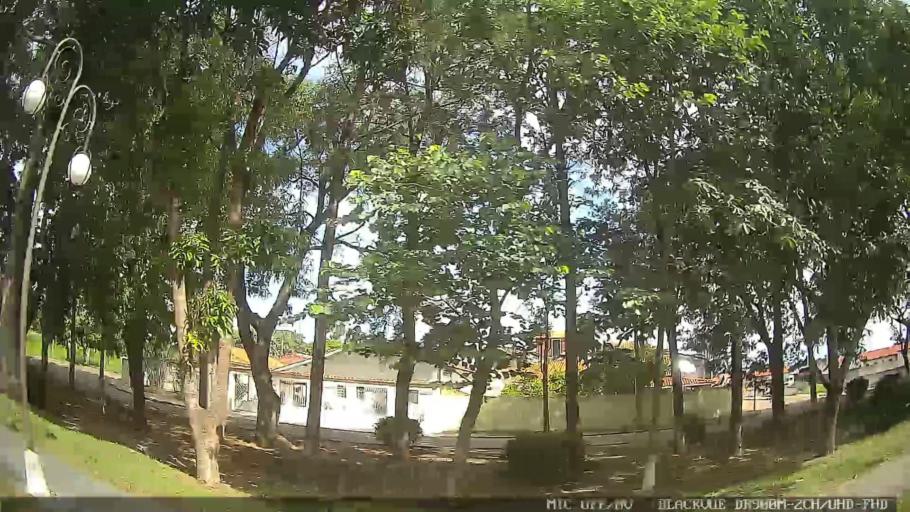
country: BR
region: Sao Paulo
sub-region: Conchas
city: Conchas
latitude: -23.0676
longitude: -47.9753
